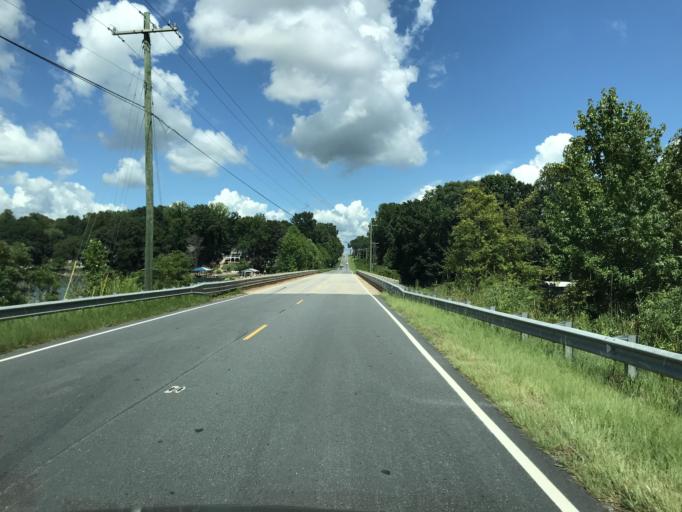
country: US
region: North Carolina
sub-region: Catawba County
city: Lake Norman of Catawba
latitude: 35.5772
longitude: -81.0025
